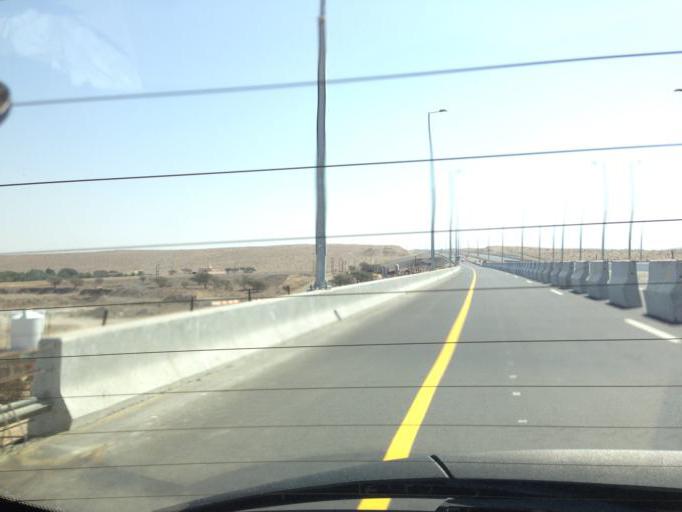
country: OM
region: Al Batinah
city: Rustaq
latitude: 23.5199
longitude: 57.6201
